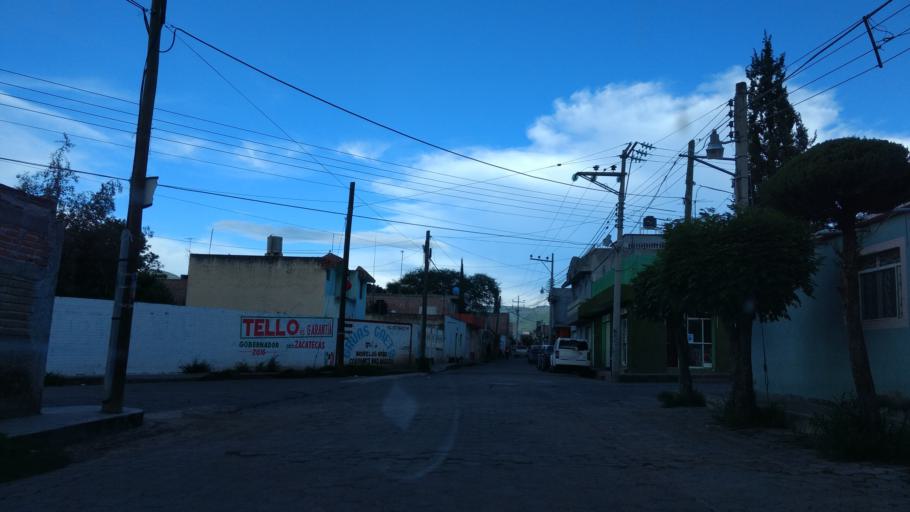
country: MX
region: Zacatecas
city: Tlaltenango de Sanchez Roman
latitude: 21.7800
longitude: -103.2997
